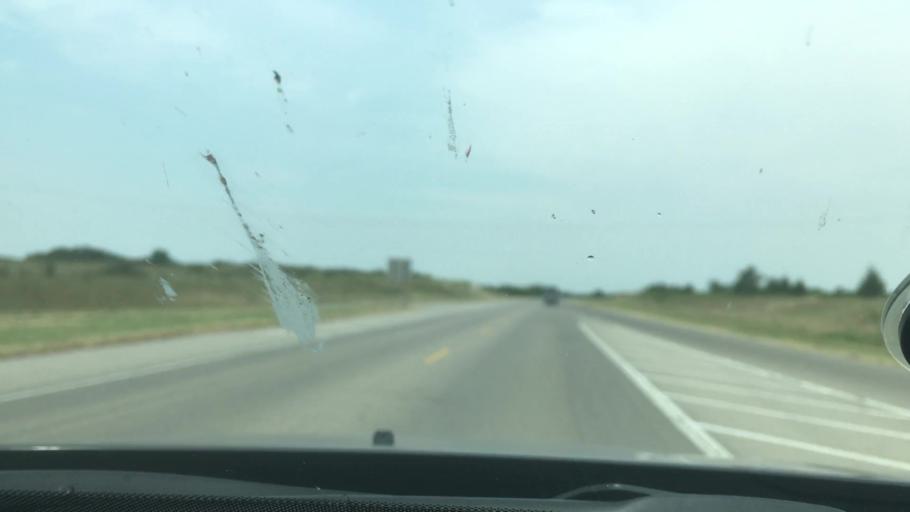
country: US
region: Oklahoma
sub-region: Pontotoc County
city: Ada
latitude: 34.6423
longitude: -96.5342
